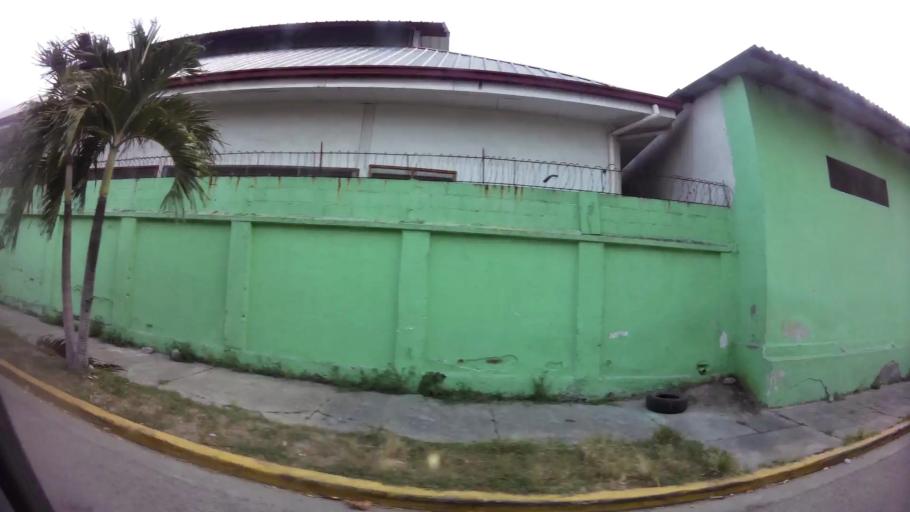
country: HN
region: Cortes
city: San Pedro Sula
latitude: 15.4931
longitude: -88.0179
